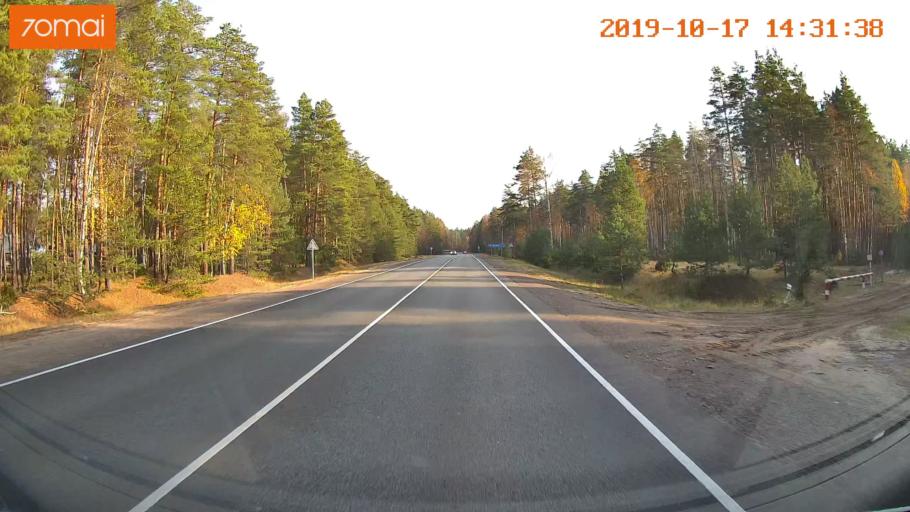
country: RU
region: Rjazan
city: Solotcha
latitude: 54.9348
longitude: 39.9671
